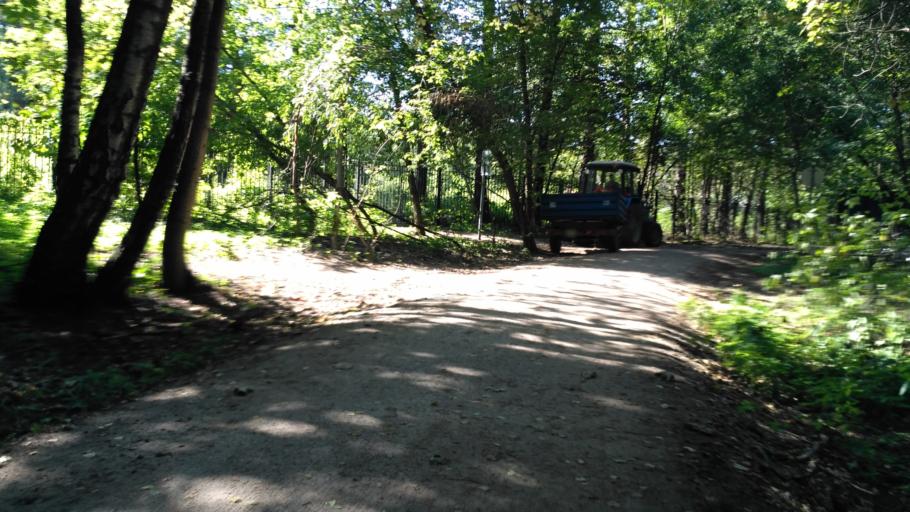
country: RU
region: Moscow
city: Metrogorodok
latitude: 55.7863
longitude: 37.7683
